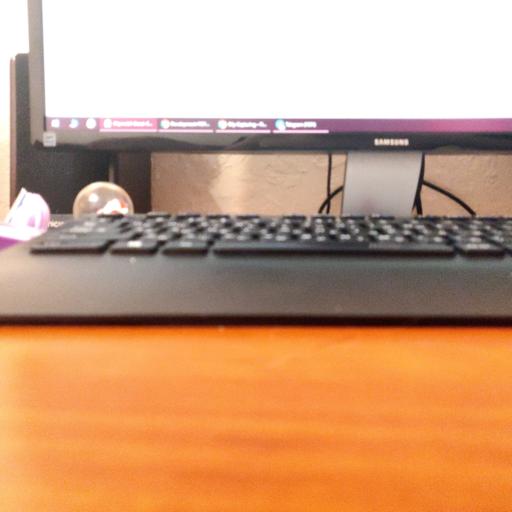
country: FI
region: Haeme
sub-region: Forssa
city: Ypaejae
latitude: 60.6410
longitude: 23.3446
